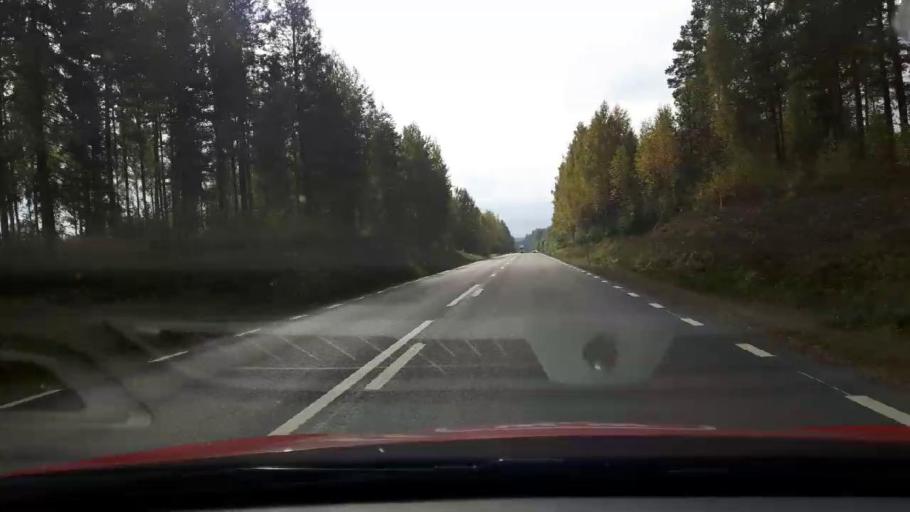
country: SE
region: Gaevleborg
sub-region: Bollnas Kommun
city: Arbra
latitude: 61.4813
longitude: 16.3656
